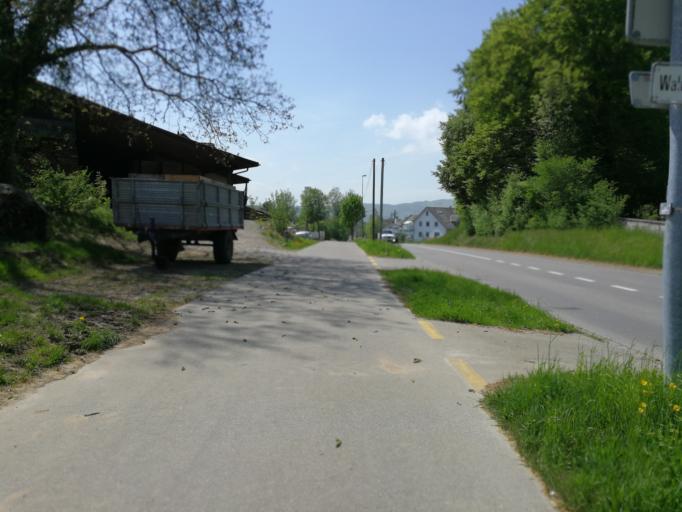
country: CH
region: Zurich
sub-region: Bezirk Hinwil
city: Gruet
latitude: 47.3041
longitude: 8.7727
